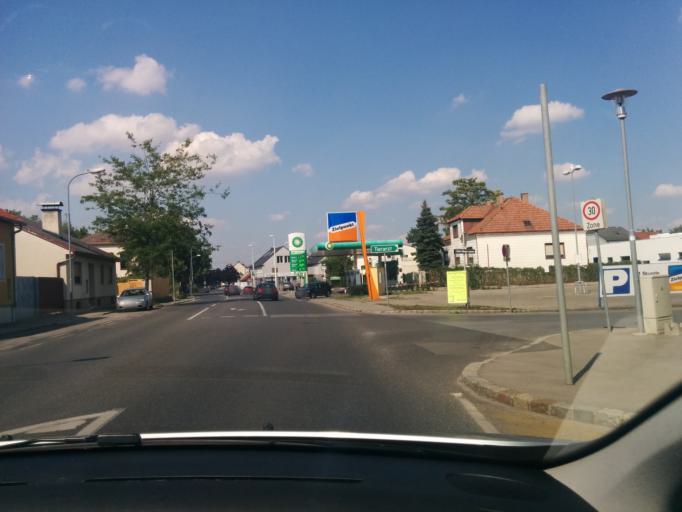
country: AT
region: Lower Austria
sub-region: Politischer Bezirk Wien-Umgebung
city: Gerasdorf bei Wien
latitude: 48.2936
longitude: 16.4672
